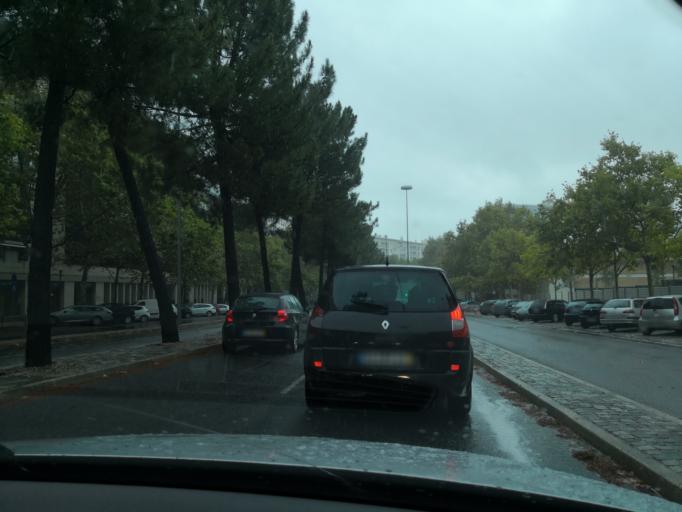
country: PT
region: Lisbon
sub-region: Loures
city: Moscavide
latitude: 38.7795
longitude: -9.0981
